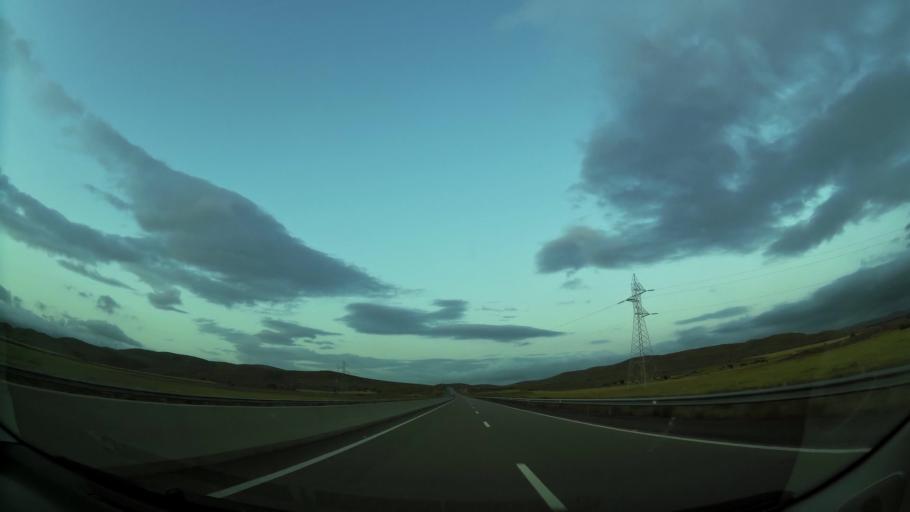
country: MA
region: Oriental
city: El Aioun
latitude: 34.6051
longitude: -2.6056
